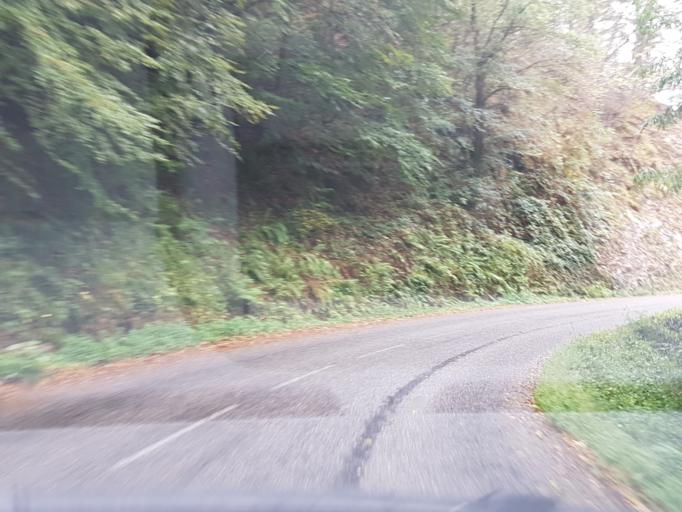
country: FR
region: Midi-Pyrenees
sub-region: Departement de l'Ariege
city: Saint-Girons
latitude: 42.9118
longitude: 1.2546
